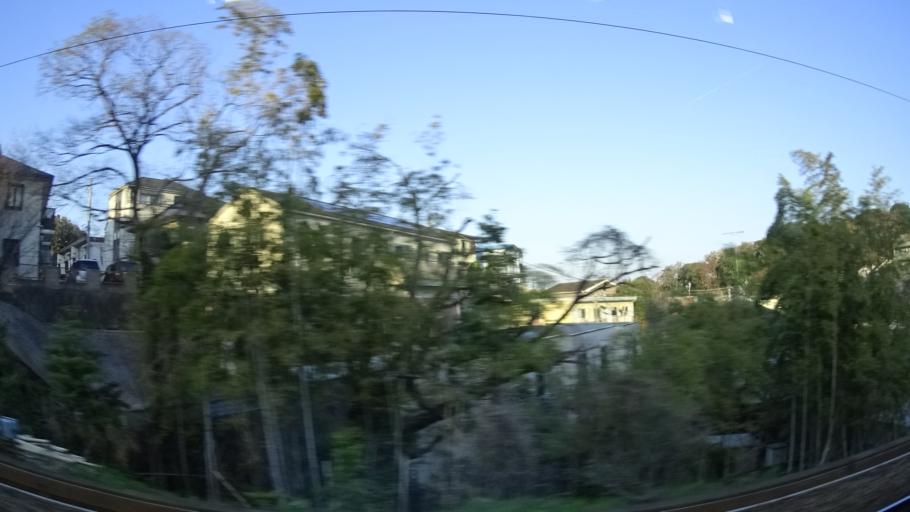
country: JP
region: Kanagawa
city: Yokohama
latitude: 35.3717
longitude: 139.6288
